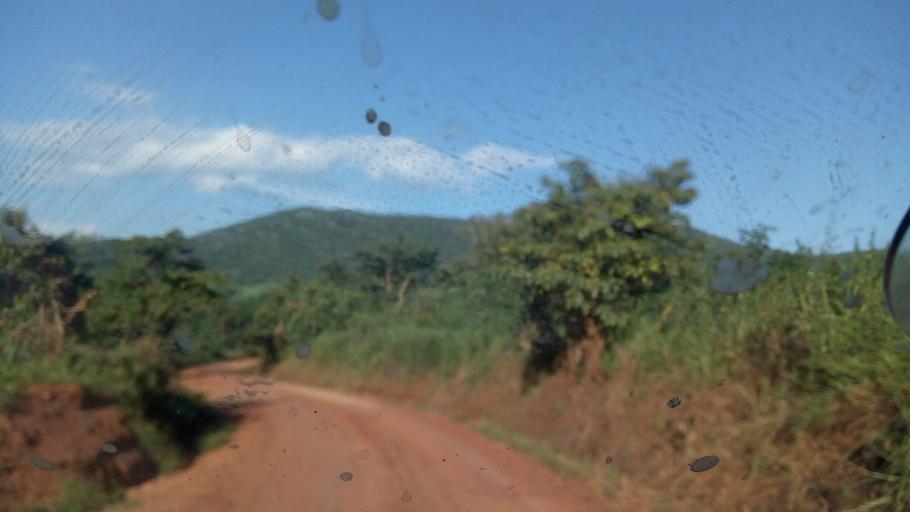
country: BI
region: Bururi
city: Rumonge
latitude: -4.2823
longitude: 28.9671
